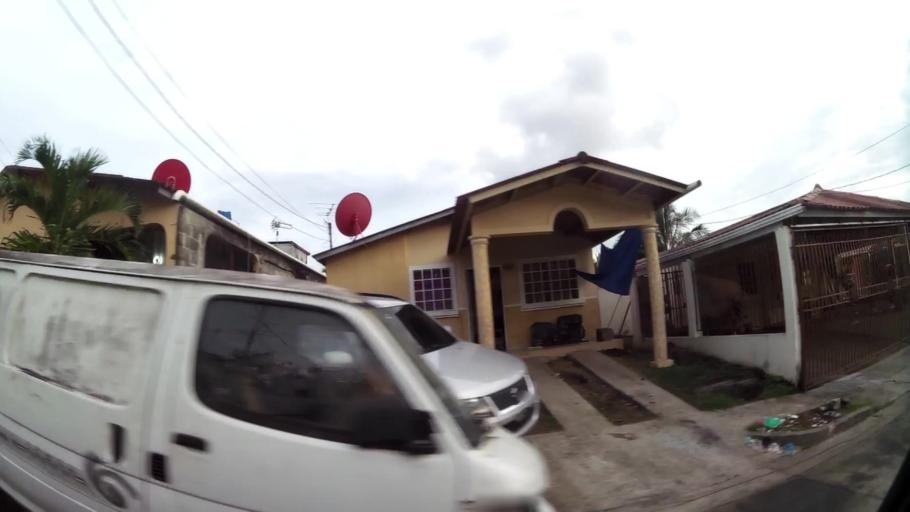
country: PA
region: Panama
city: Tocumen
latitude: 9.0952
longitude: -79.3968
